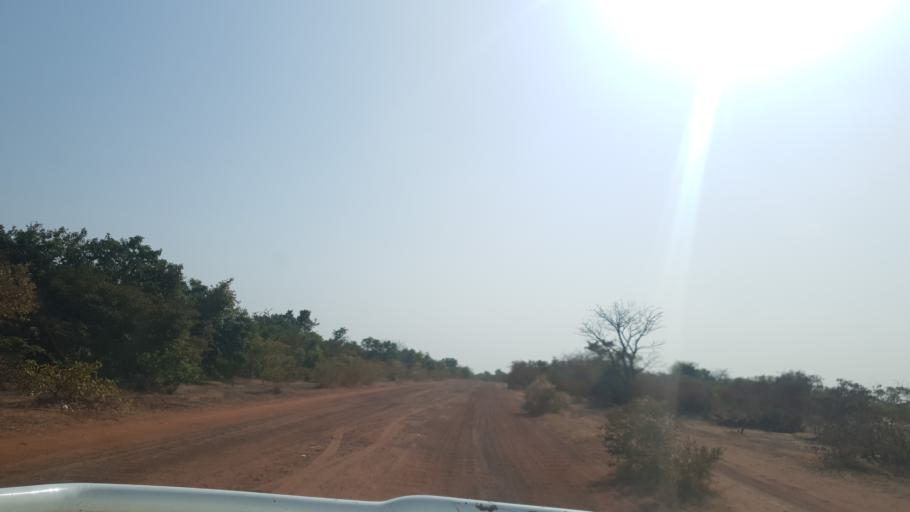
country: ML
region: Koulikoro
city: Dioila
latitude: 12.6719
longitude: -6.7070
